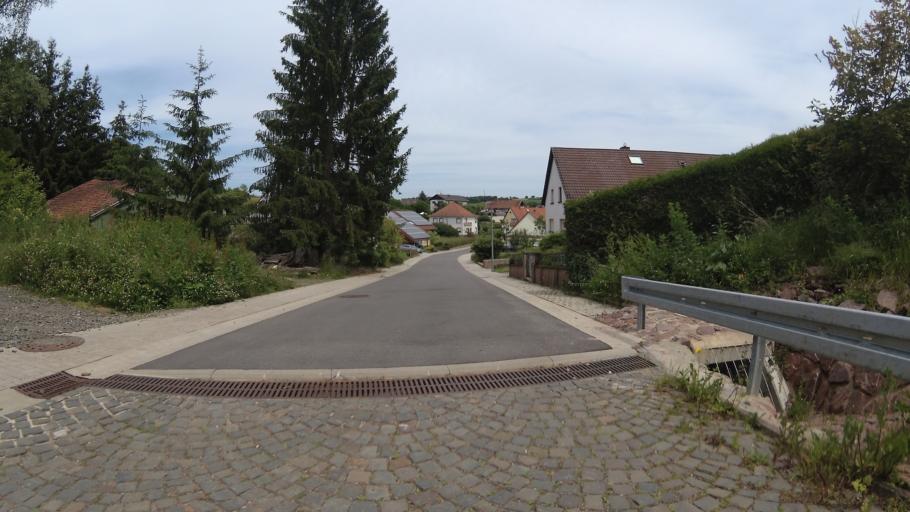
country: DE
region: Rheinland-Pfalz
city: Breitenbach
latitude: 49.4192
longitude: 7.2325
